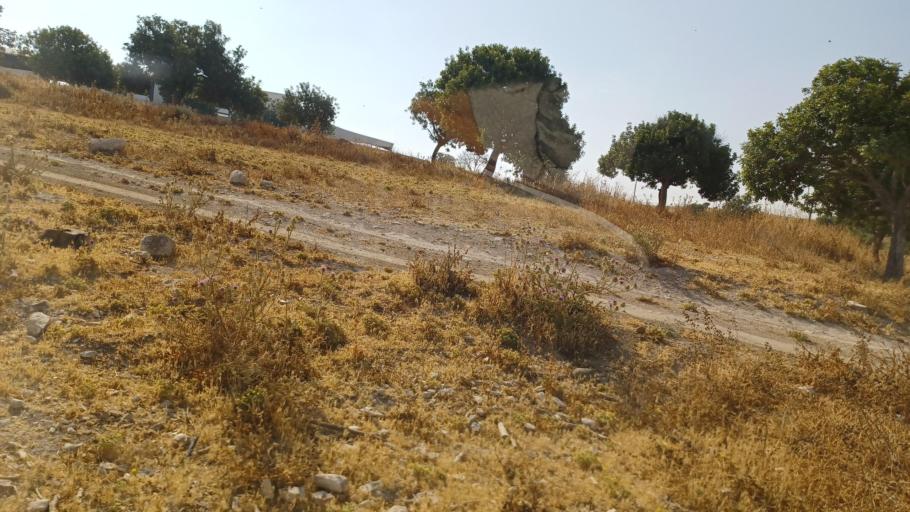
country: CY
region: Lefkosia
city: Lympia
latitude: 34.9879
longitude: 33.4734
